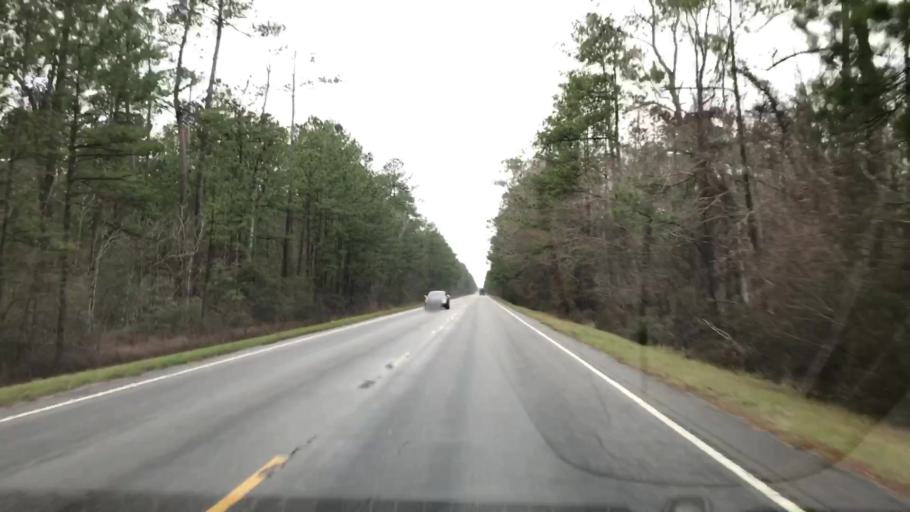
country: US
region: South Carolina
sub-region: Berkeley County
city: Saint Stephen
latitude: 33.2880
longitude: -79.8303
